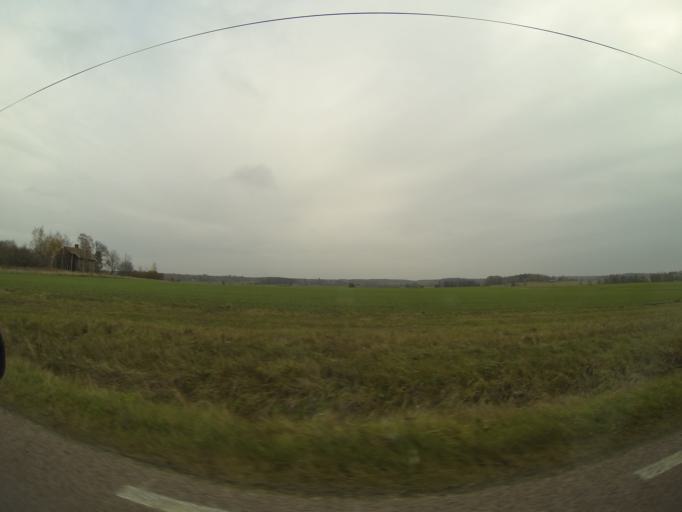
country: SE
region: Vaestmanland
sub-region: Vasteras
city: Skultuna
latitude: 59.6597
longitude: 16.4596
